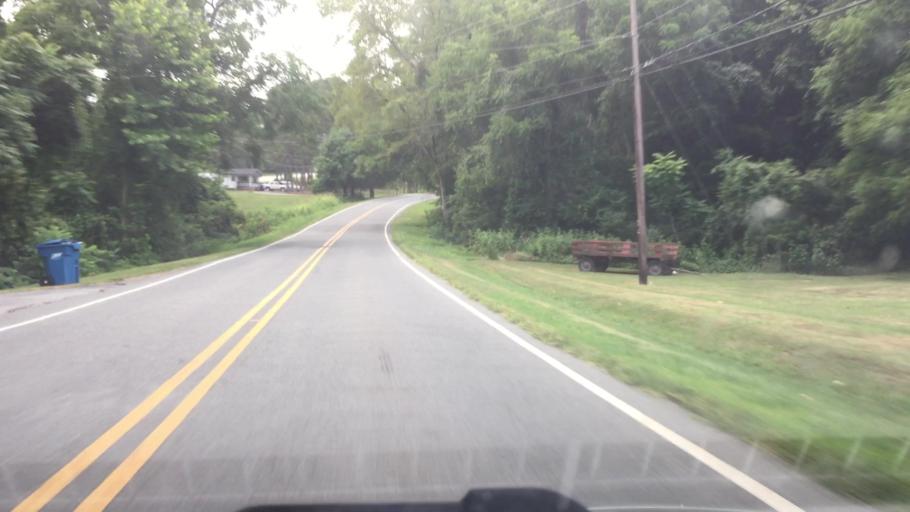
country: US
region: North Carolina
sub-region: Rowan County
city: Enochville
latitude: 35.4676
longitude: -80.7300
